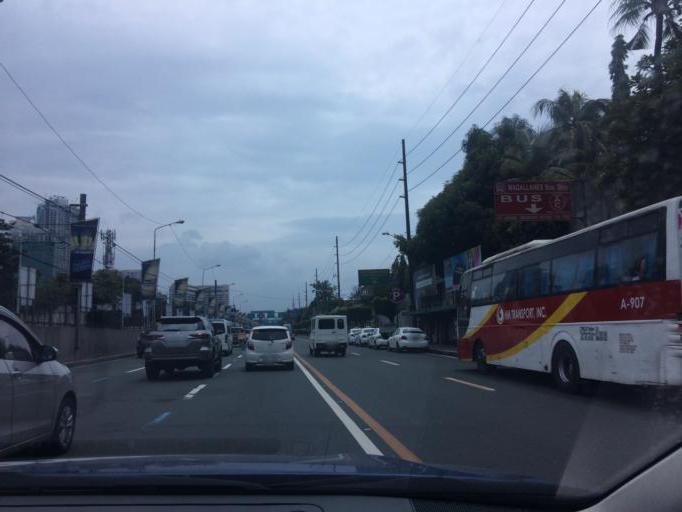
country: PH
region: Metro Manila
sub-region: Makati City
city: Makati City
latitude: 14.5433
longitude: 121.0213
